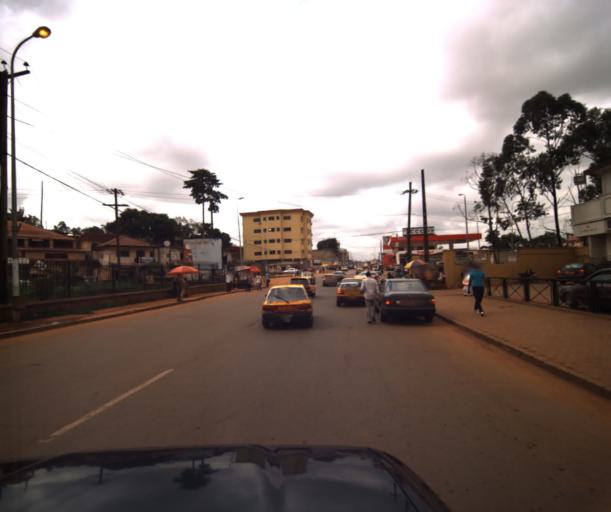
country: CM
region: Centre
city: Yaounde
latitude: 3.8583
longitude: 11.5220
